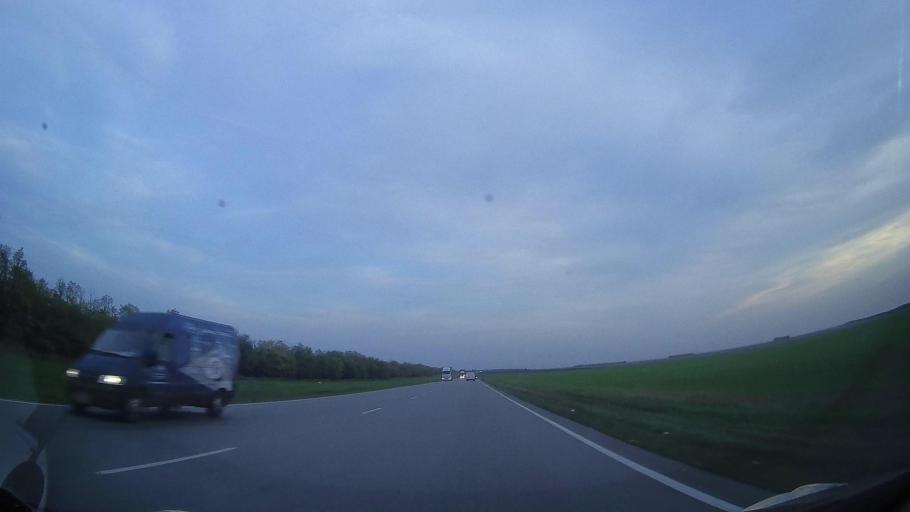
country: RU
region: Rostov
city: Kagal'nitskaya
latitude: 46.9102
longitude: 40.1143
